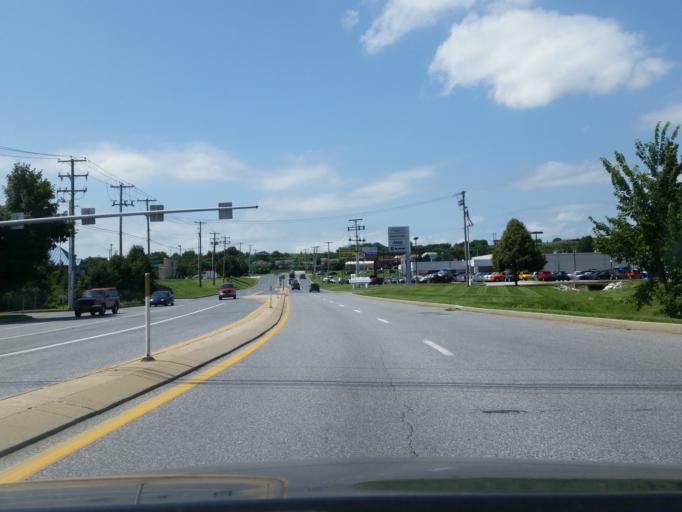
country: US
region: Pennsylvania
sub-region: York County
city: North York
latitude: 39.9791
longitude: -76.7584
